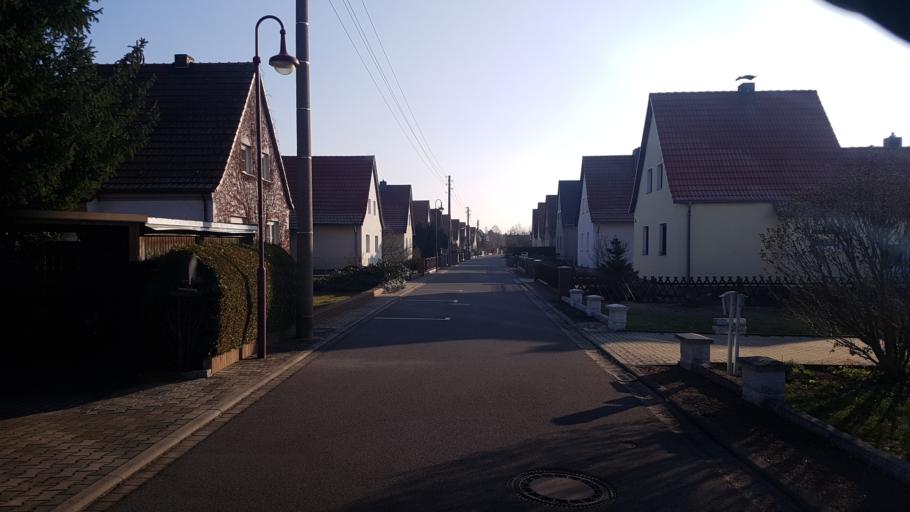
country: DE
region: Brandenburg
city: Lauchhammer
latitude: 51.4735
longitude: 13.7665
